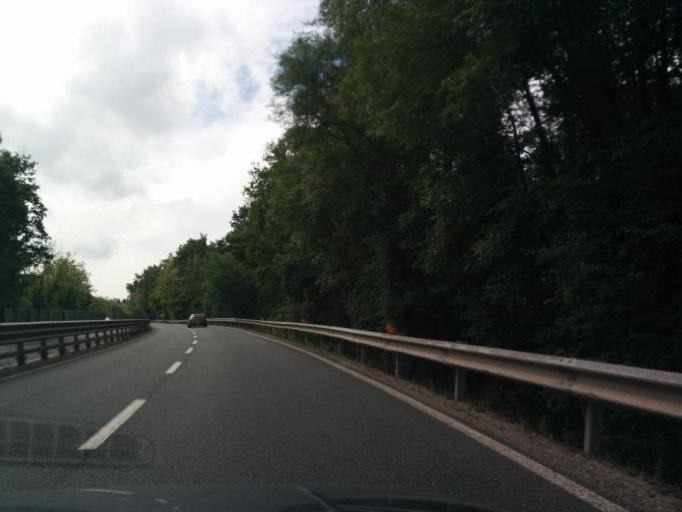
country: IT
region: Tuscany
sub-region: Province of Florence
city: Sambuca
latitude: 43.5710
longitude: 11.2078
